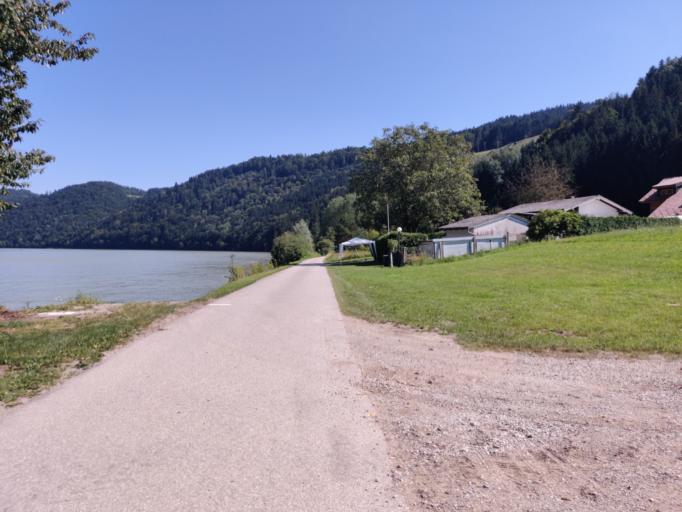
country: AT
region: Upper Austria
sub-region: Politischer Bezirk Rohrbach
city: Pfarrkirchen im Muehlkreis
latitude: 48.4480
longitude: 13.8663
